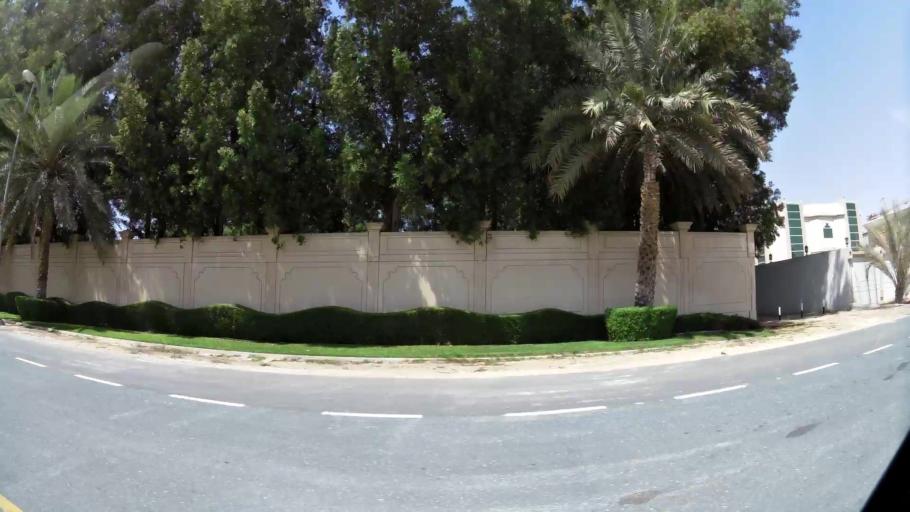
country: AE
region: Dubai
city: Dubai
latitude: 25.1045
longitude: 55.2255
